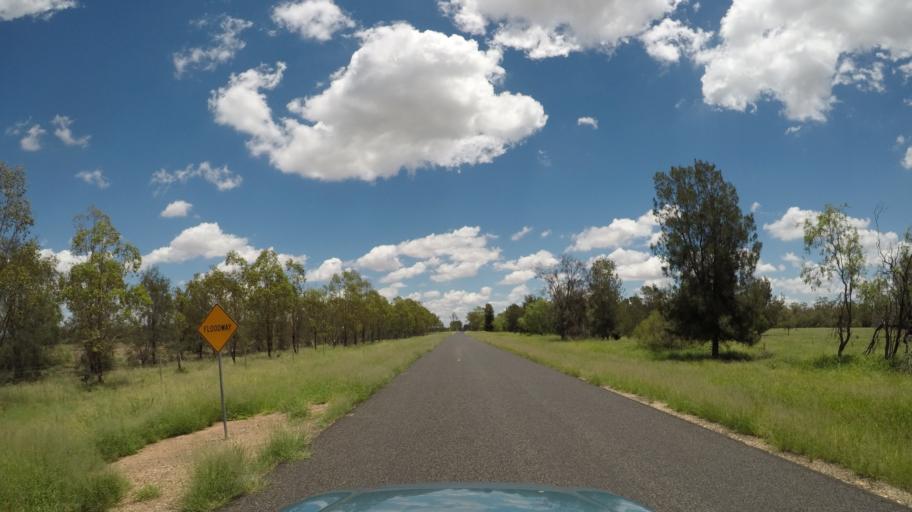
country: AU
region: Queensland
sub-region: Goondiwindi
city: Goondiwindi
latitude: -28.1593
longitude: 150.1239
